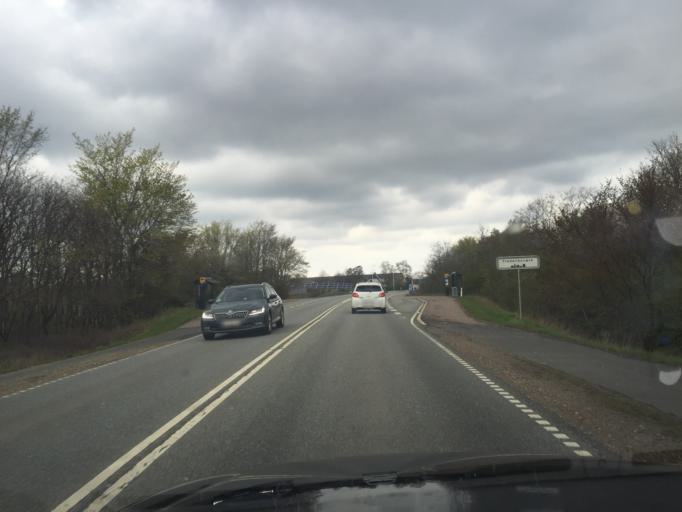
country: DK
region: Capital Region
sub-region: Halsnaes Kommune
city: Frederiksvaerk
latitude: 55.9619
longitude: 12.0320
